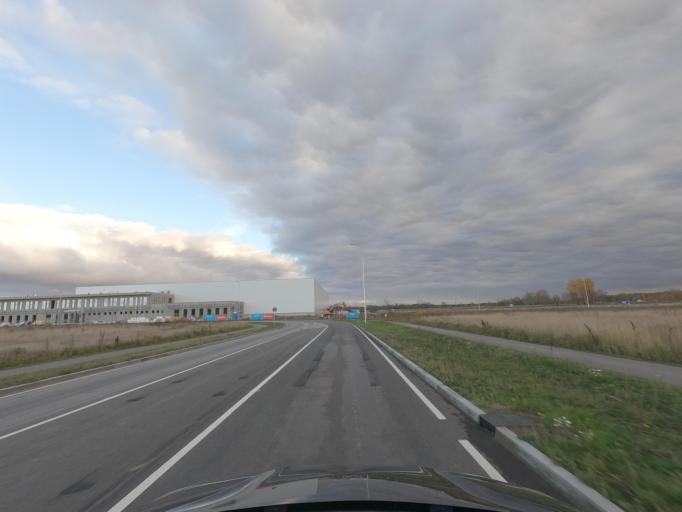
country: EE
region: Harju
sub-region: Saue vald
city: Laagri
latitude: 59.3346
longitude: 24.5977
